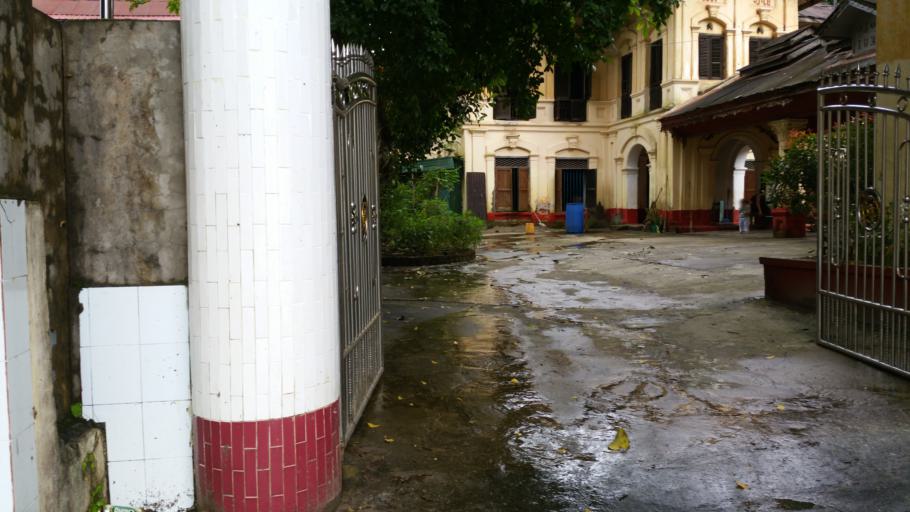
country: MM
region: Mon
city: Mawlamyine
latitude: 16.4883
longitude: 97.6249
